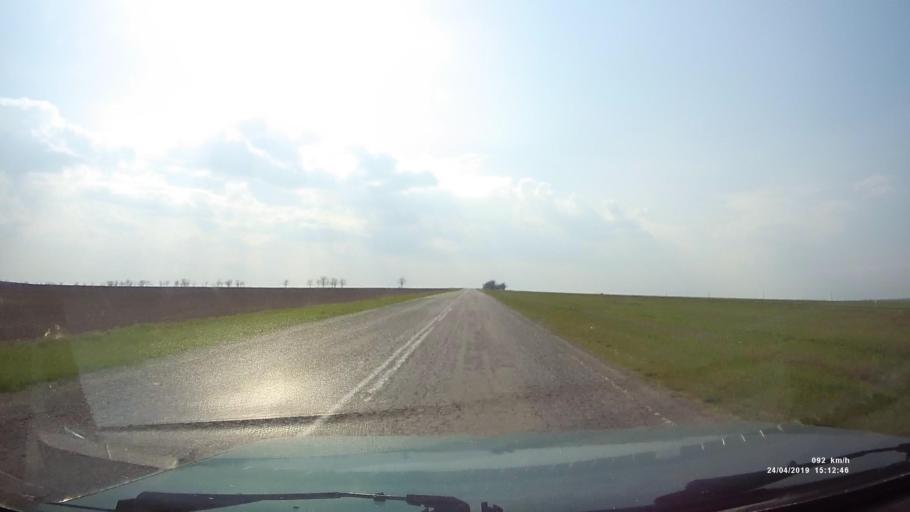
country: RU
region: Rostov
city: Remontnoye
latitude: 46.5464
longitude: 43.2936
